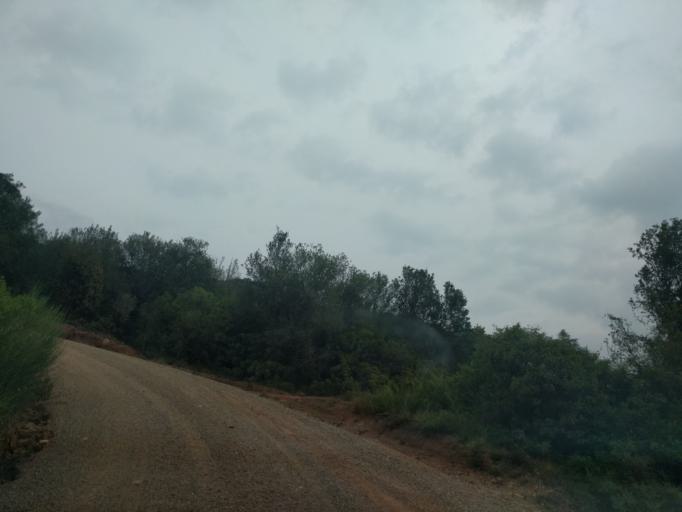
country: ES
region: Catalonia
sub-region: Provincia de Girona
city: la Cellera de Ter
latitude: 42.0094
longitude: 2.6342
